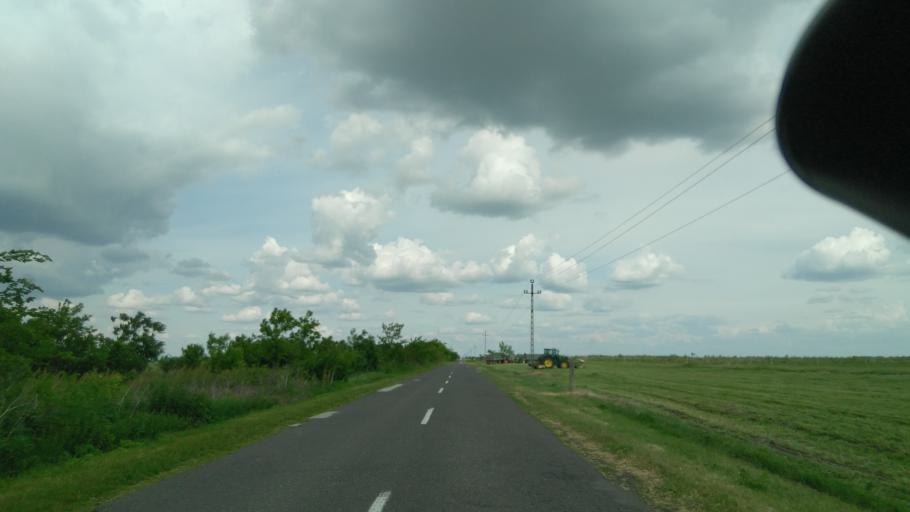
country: HU
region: Bekes
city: Mezohegyes
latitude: 46.3112
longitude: 20.8610
